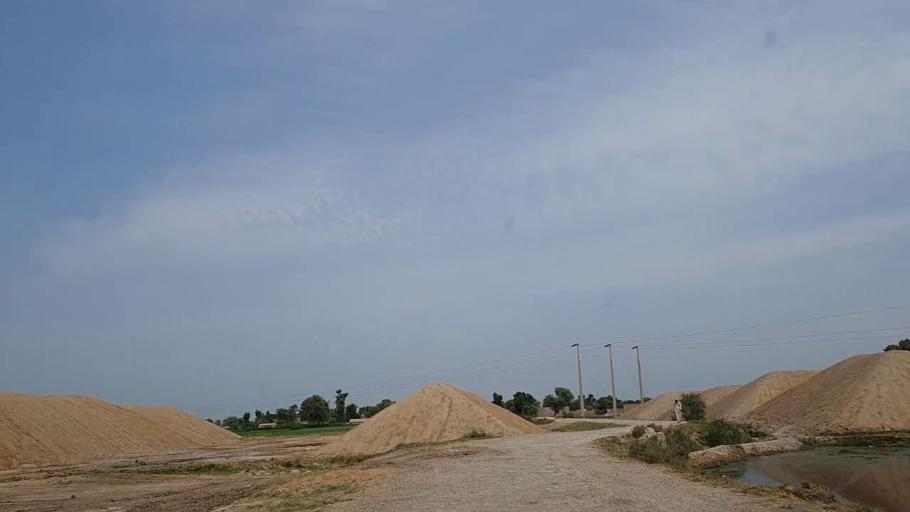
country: PK
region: Sindh
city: Khanpur
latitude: 27.8578
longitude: 69.4193
